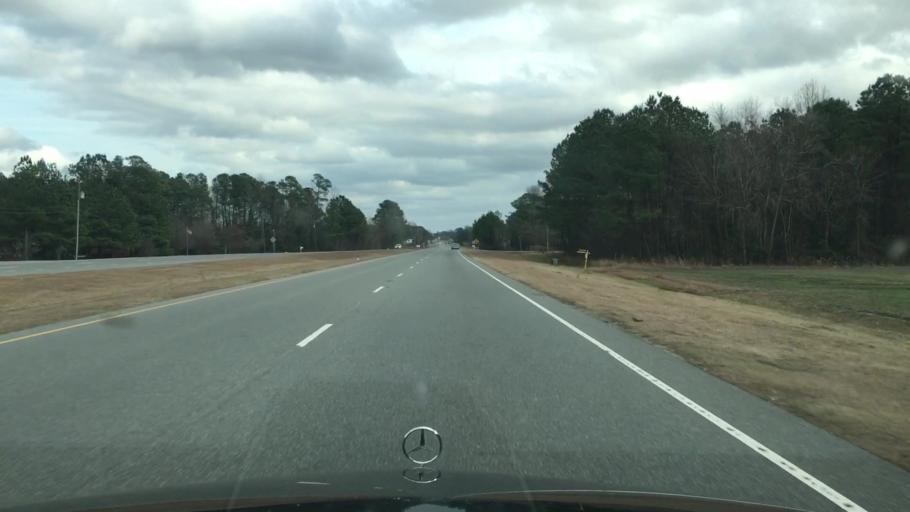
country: US
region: North Carolina
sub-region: Duplin County
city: Beulaville
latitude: 34.9296
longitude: -77.8125
